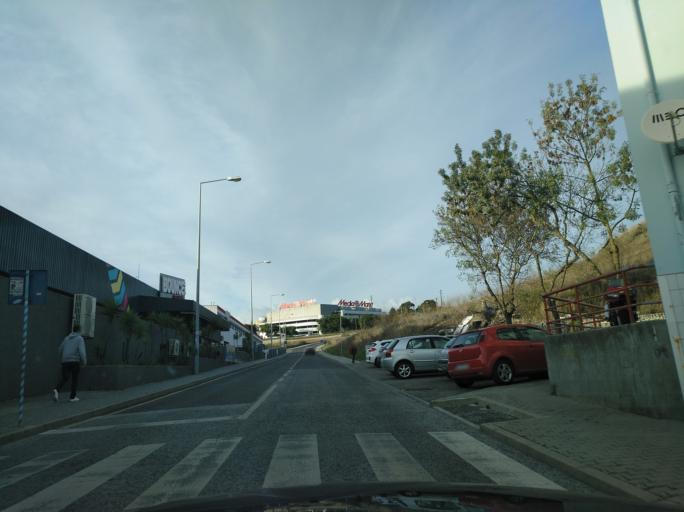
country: PT
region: Lisbon
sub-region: Oeiras
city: Linda-a-Velha
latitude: 38.7260
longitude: -9.2222
